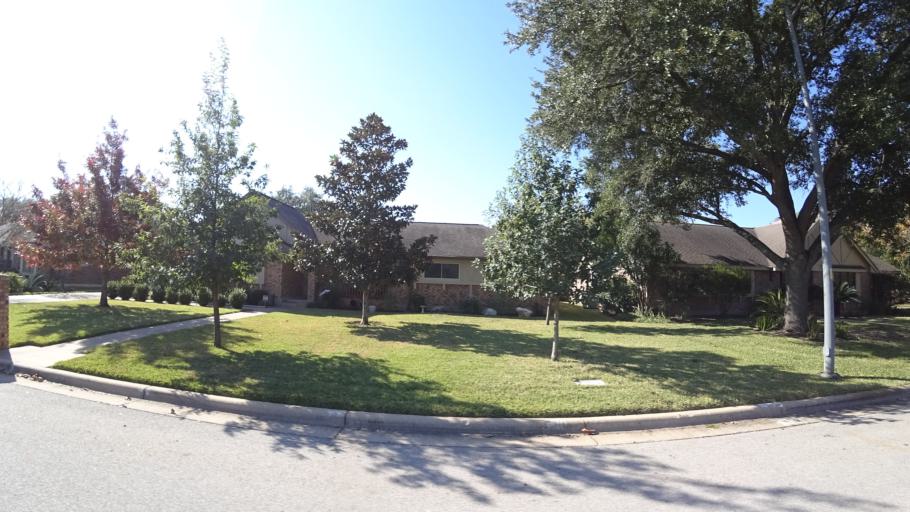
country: US
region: Texas
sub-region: Travis County
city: Shady Hollow
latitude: 30.2215
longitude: -97.8530
